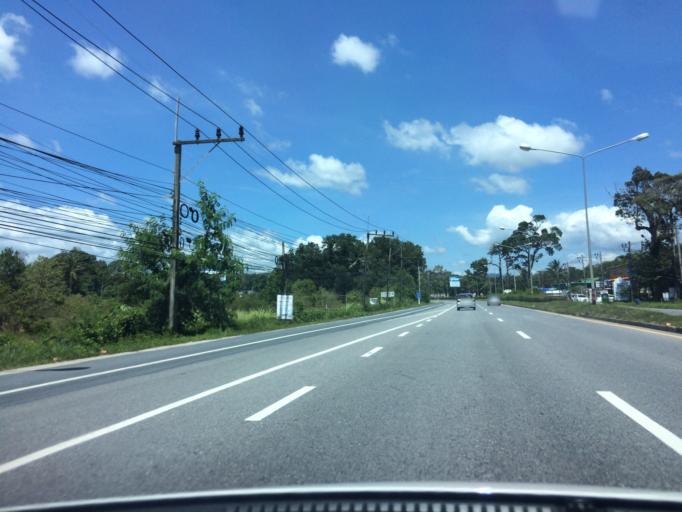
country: TH
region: Phangnga
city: Thai Mueang
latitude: 8.2250
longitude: 98.2994
